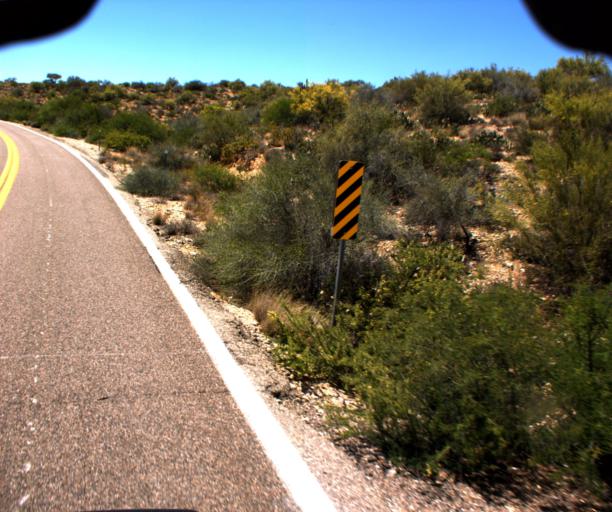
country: US
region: Arizona
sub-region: Yavapai County
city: Bagdad
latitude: 34.5225
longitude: -113.1077
